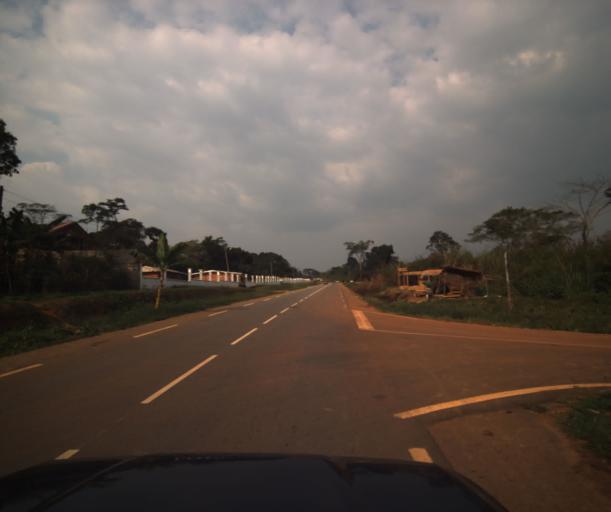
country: CM
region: Centre
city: Mbankomo
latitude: 3.7053
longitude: 11.3758
